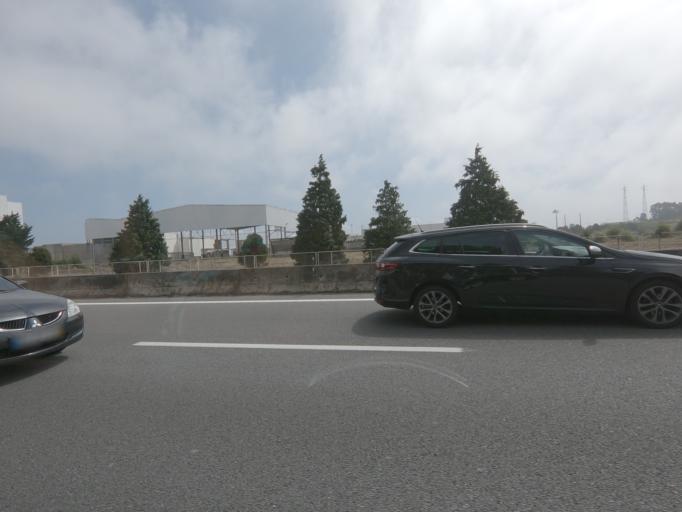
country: PT
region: Porto
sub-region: Matosinhos
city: Santa Cruz do Bispo
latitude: 41.2125
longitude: -8.6906
